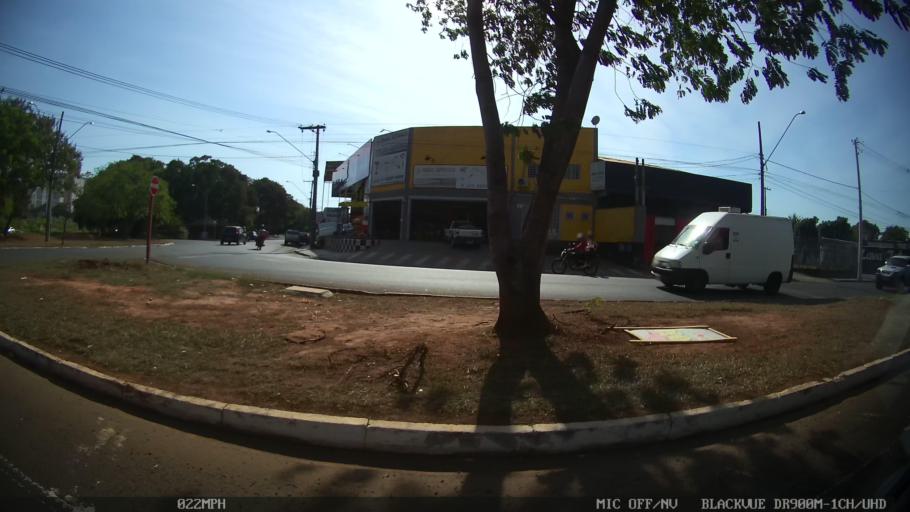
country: BR
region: Sao Paulo
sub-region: Sao Jose Do Rio Preto
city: Sao Jose do Rio Preto
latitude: -20.7967
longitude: -49.3992
